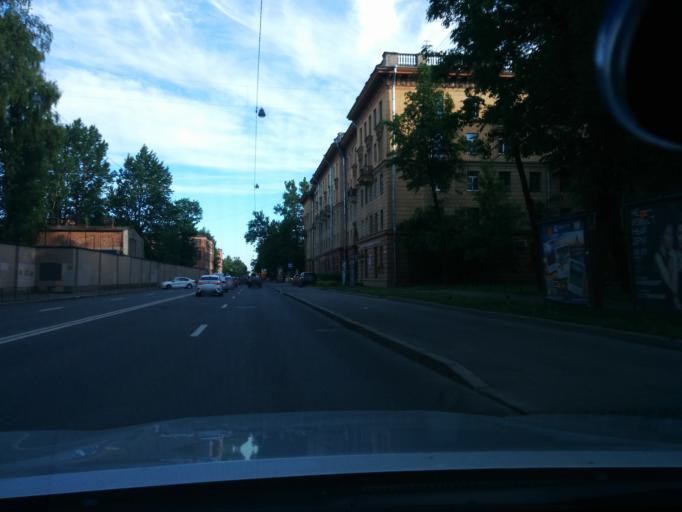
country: RU
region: Leningrad
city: Sampsonievskiy
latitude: 59.9821
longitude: 30.3361
